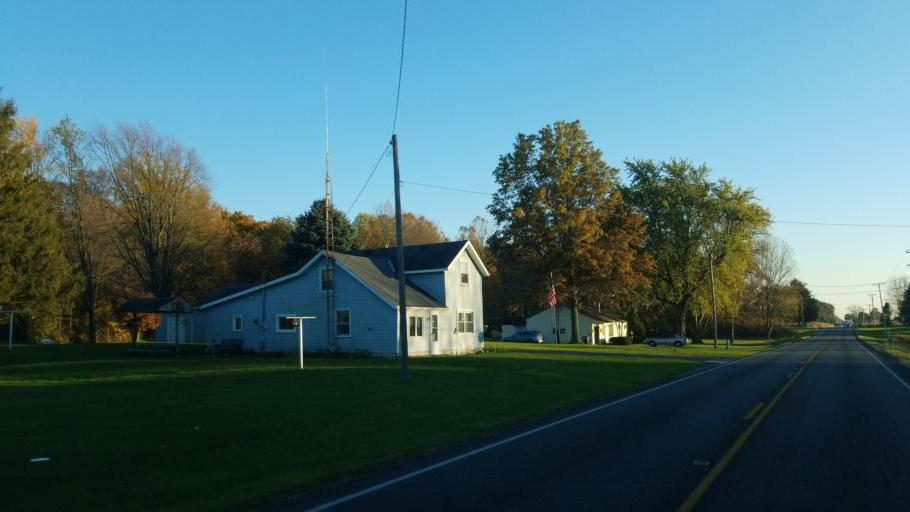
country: US
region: Ohio
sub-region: Sandusky County
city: Clyde
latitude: 41.2701
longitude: -82.9752
